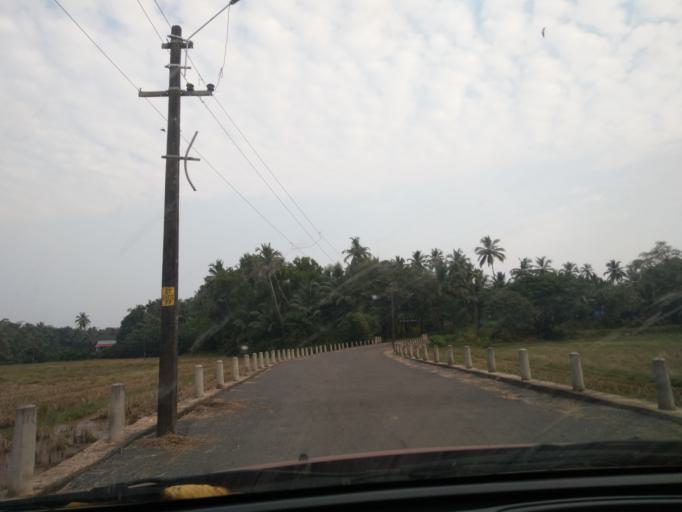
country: IN
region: Goa
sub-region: South Goa
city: Varca
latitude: 15.2257
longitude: 73.9538
